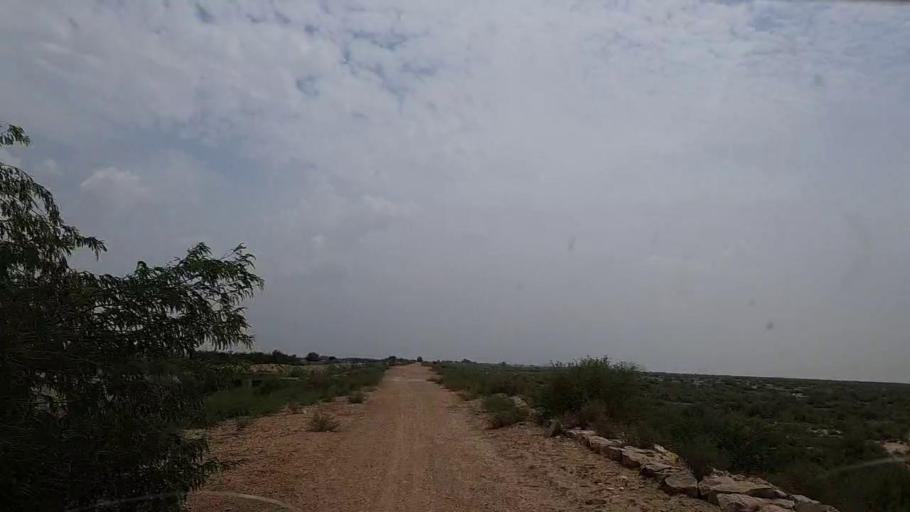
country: PK
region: Sindh
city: Phulji
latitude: 26.8399
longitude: 67.6180
